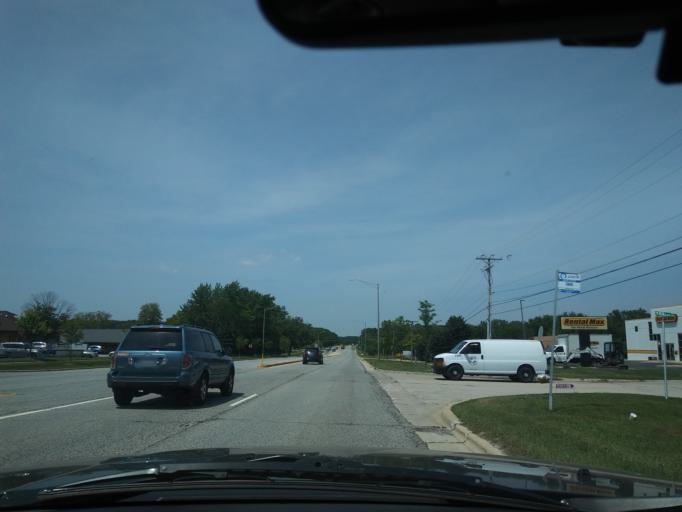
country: US
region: Illinois
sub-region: Cook County
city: Tinley Park
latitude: 41.6130
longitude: -87.7944
